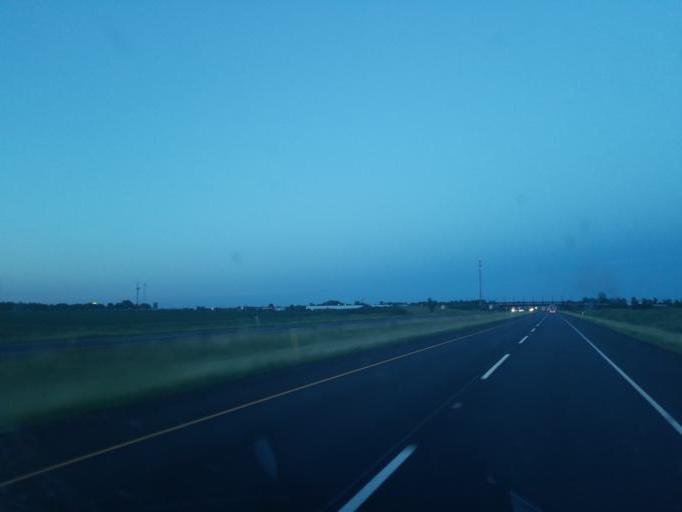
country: US
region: Michigan
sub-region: Berrien County
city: Buchanan
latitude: 41.7303
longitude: -86.3543
